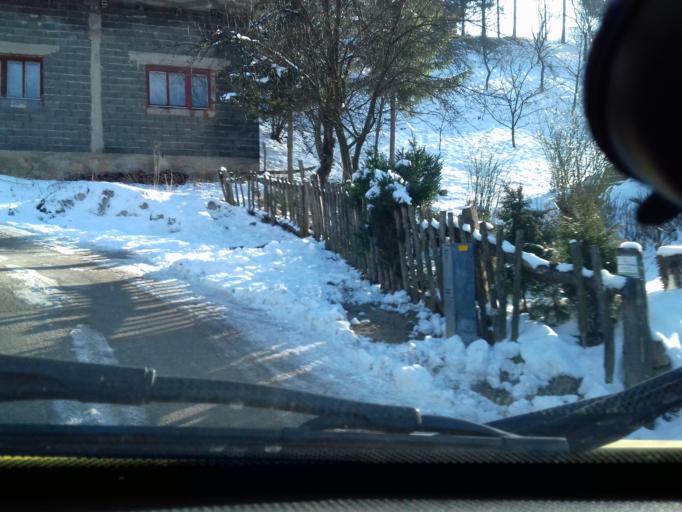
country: BA
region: Federation of Bosnia and Herzegovina
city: Zenica
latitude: 44.1789
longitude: 17.8791
